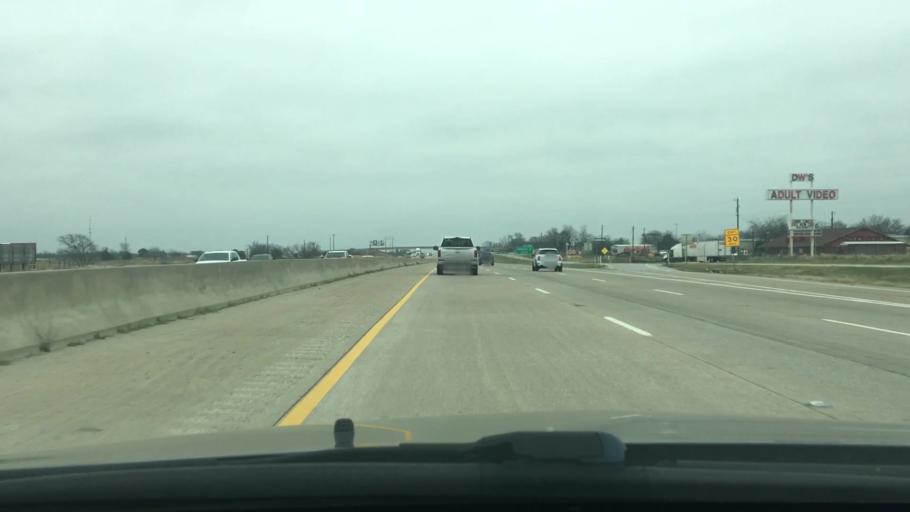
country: US
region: Texas
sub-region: Ellis County
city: Ennis
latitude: 32.2631
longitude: -96.5068
